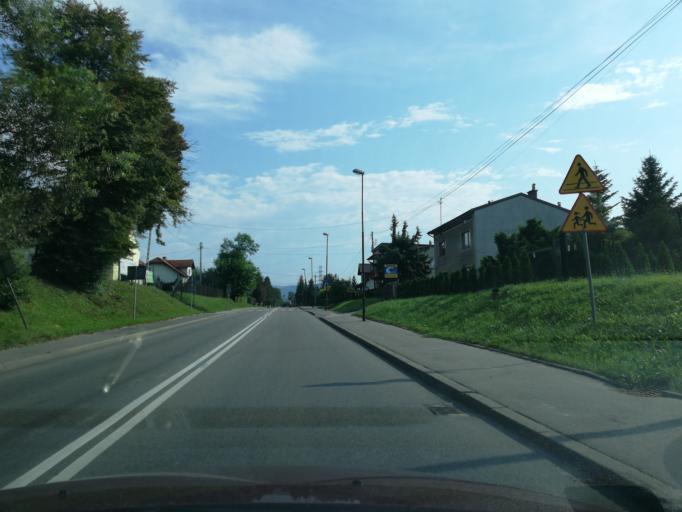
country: PL
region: Lesser Poland Voivodeship
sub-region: Powiat nowosadecki
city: Nawojowa
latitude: 49.5880
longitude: 20.7251
